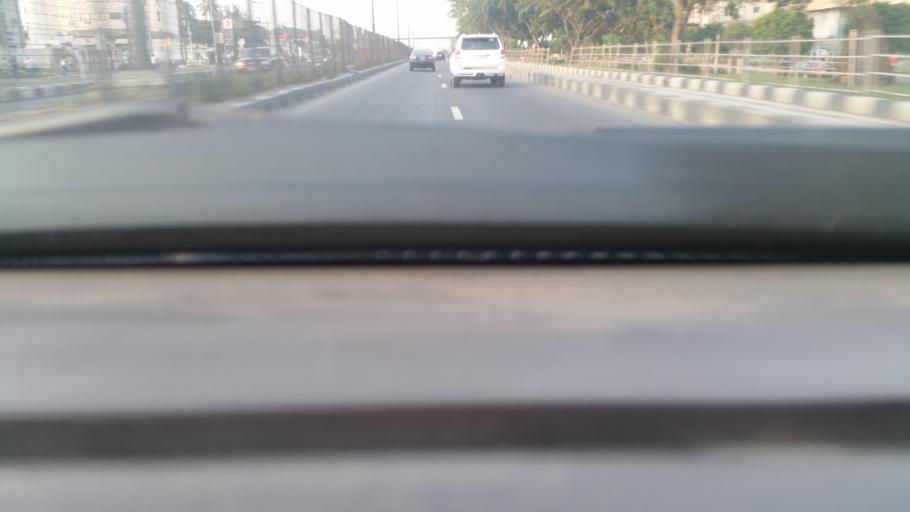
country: NG
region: Lagos
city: Somolu
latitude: 6.5389
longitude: 3.3672
